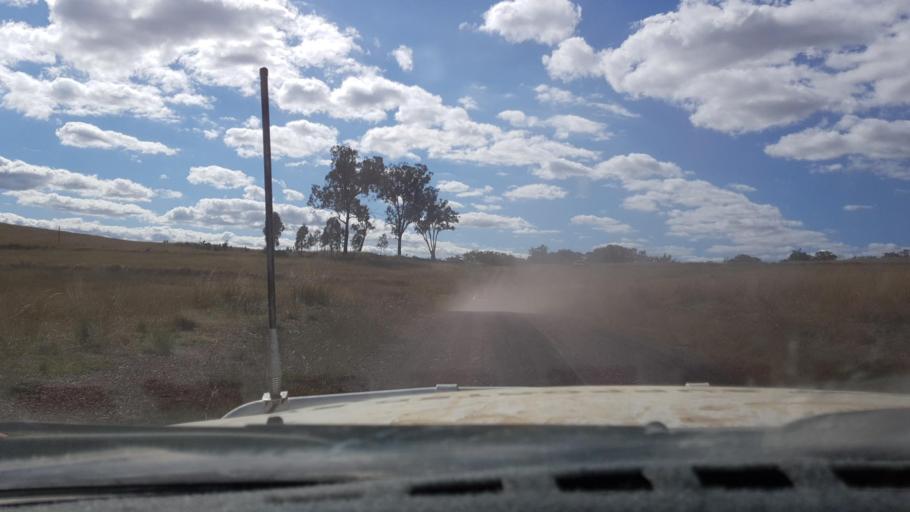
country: AU
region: New South Wales
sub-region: Tamworth Municipality
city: Manilla
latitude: -30.4574
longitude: 150.7802
